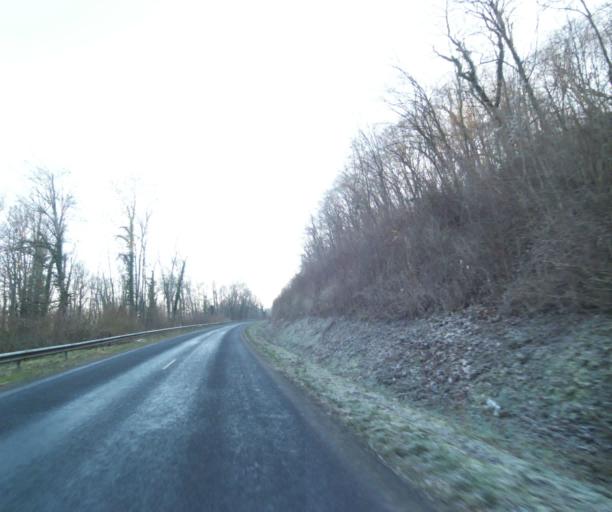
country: FR
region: Champagne-Ardenne
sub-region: Departement de la Haute-Marne
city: Bienville
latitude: 48.5567
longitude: 5.0640
